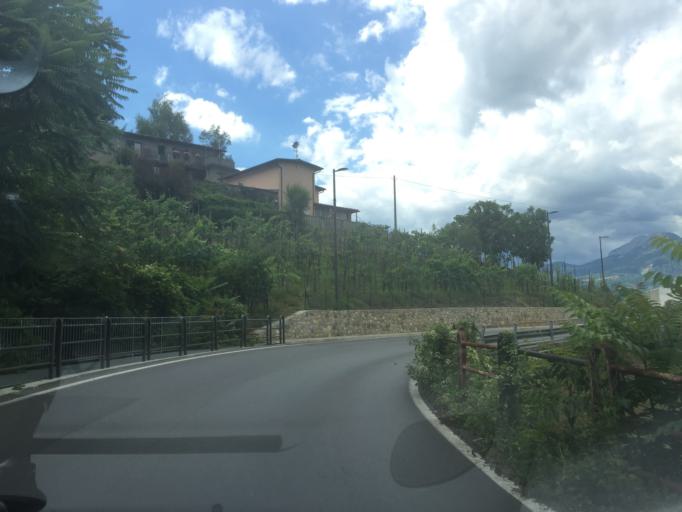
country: IT
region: Tuscany
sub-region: Provincia di Lucca
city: Castelnuovo di Garfagnana
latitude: 44.1156
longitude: 10.3974
